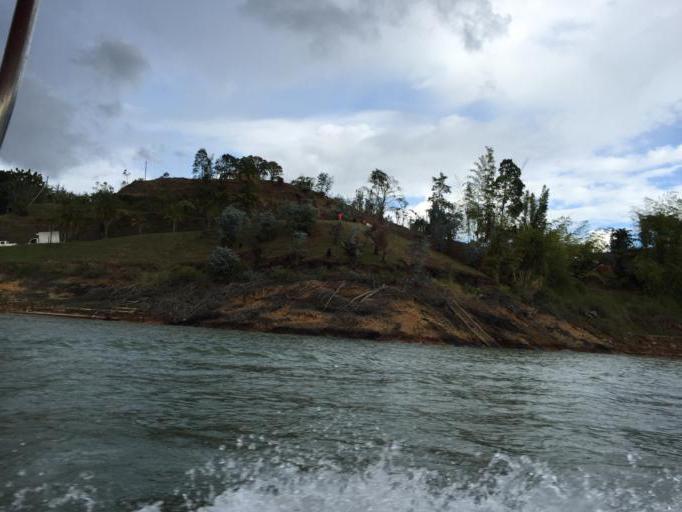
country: CO
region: Antioquia
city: Guatape
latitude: 6.2362
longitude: -75.2210
